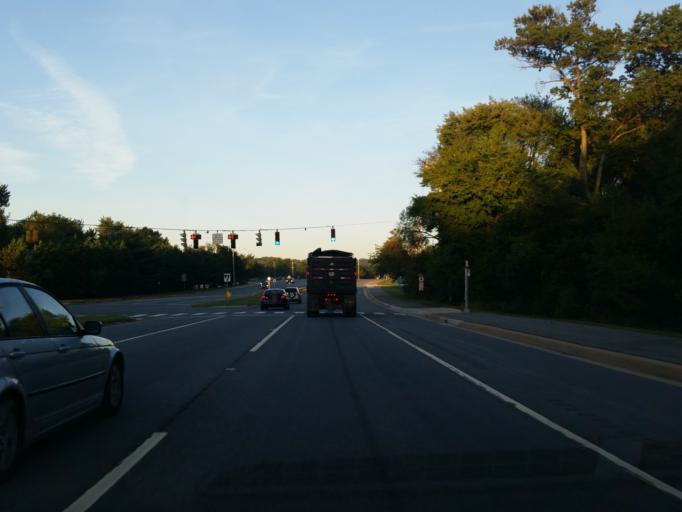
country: US
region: Delaware
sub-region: New Castle County
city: Brookside
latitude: 39.6593
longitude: -75.7436
